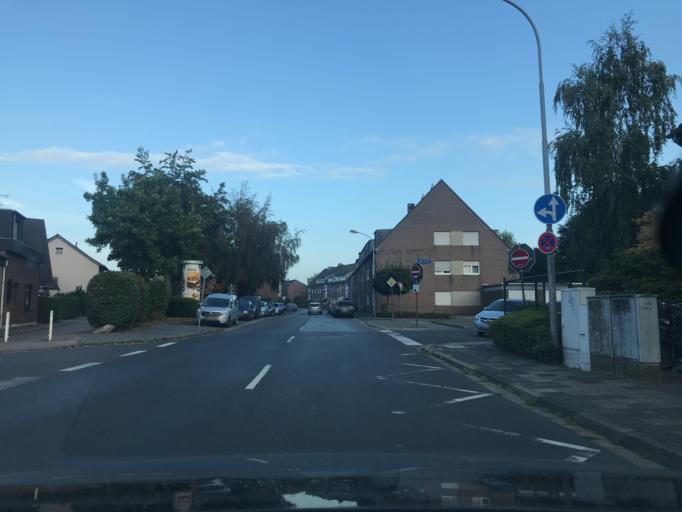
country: DE
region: North Rhine-Westphalia
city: Tonisvorst
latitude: 51.3238
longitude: 6.4981
